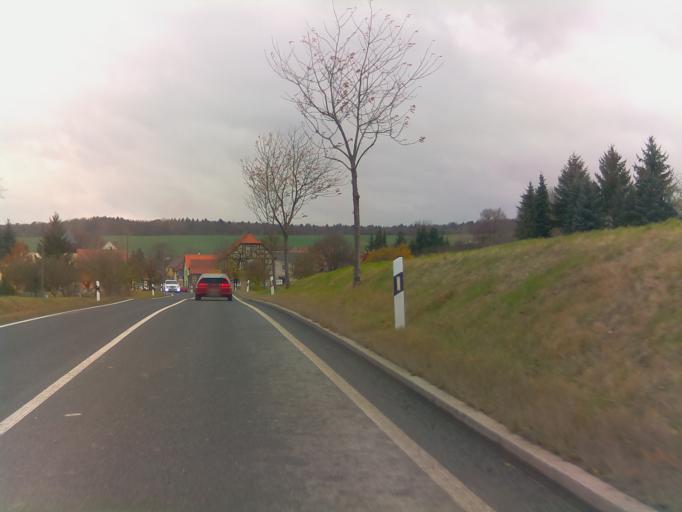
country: DE
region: Thuringia
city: Tonndorf
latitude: 50.9188
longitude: 11.2166
